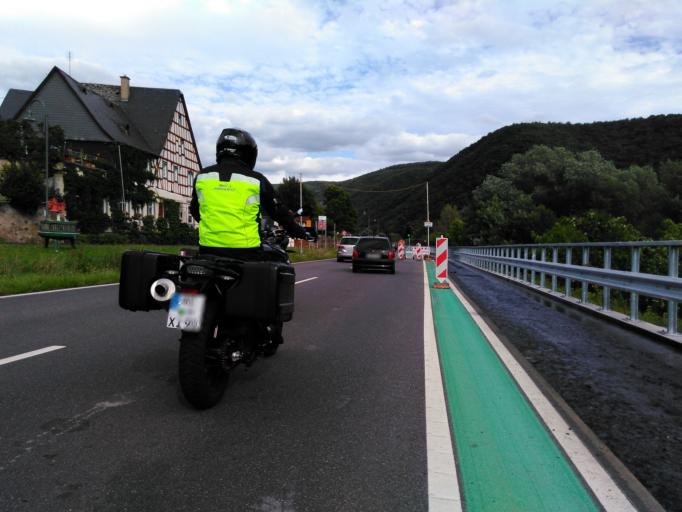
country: DE
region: Rheinland-Pfalz
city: Lutz
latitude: 50.1843
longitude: 7.3377
